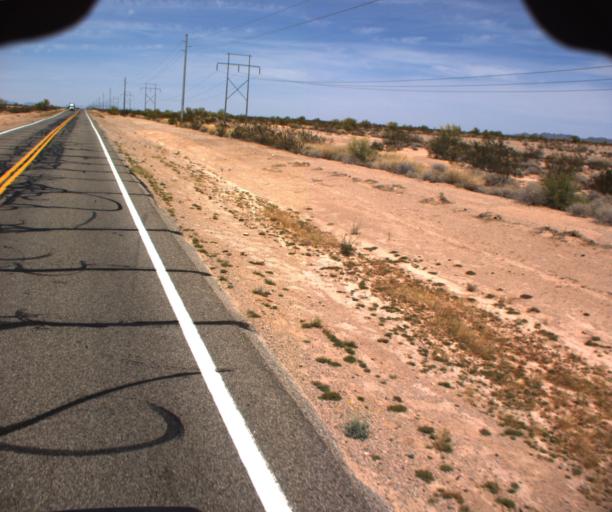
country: US
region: Arizona
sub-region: La Paz County
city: Quartzsite
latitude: 33.7939
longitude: -114.2170
